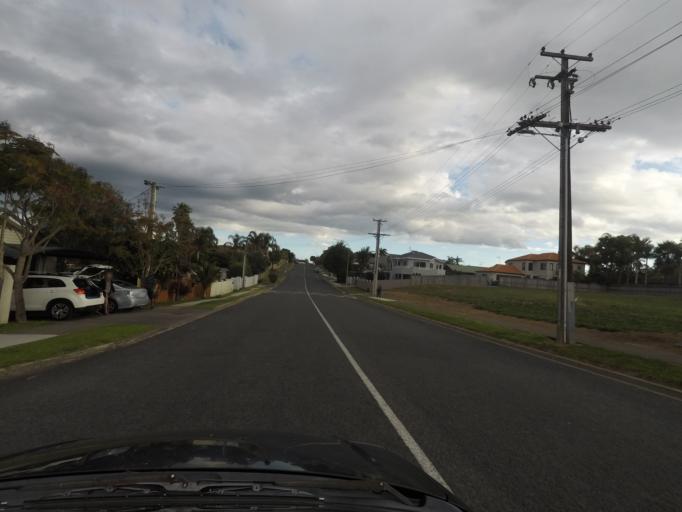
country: NZ
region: Auckland
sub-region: Auckland
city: Rosebank
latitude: -36.8023
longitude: 174.6454
